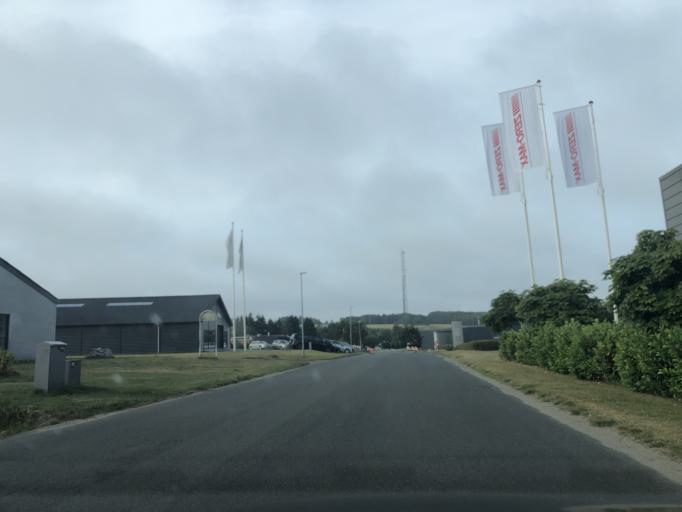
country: DK
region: Central Jutland
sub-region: Silkeborg Kommune
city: Svejbaek
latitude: 56.1578
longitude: 9.6465
